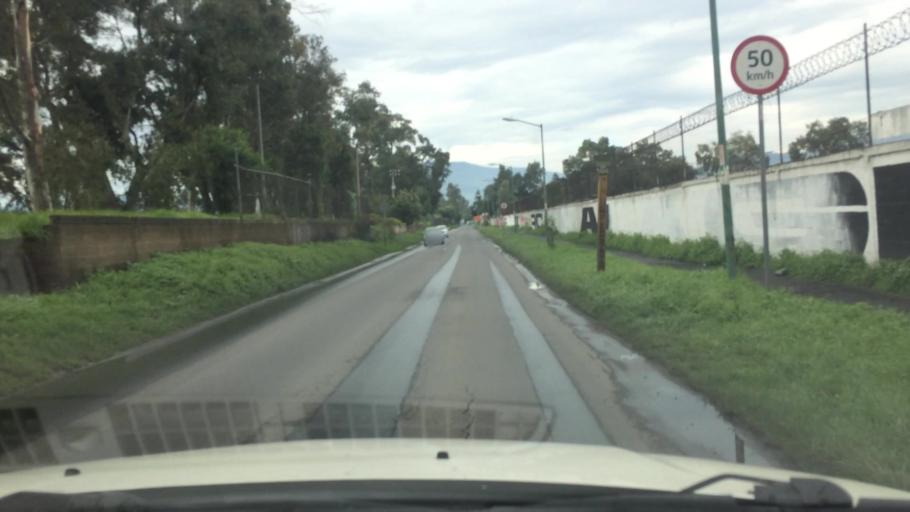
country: MX
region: Mexico City
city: Xochimilco
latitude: 19.3057
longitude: -99.1004
